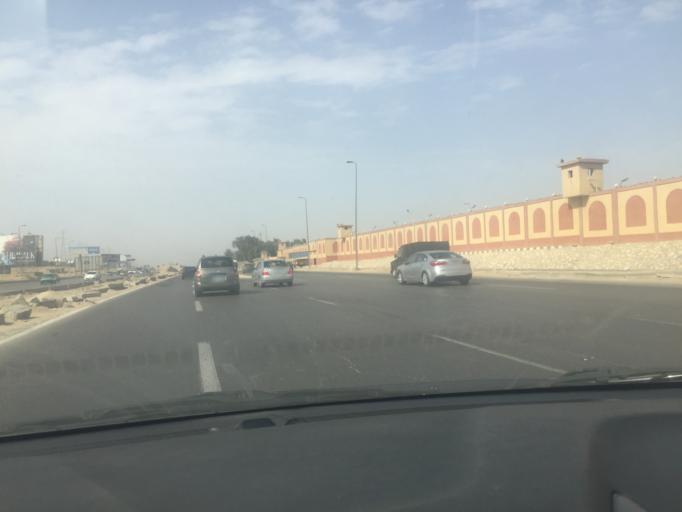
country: EG
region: Muhafazat al Qalyubiyah
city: Al Khankah
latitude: 30.0828
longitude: 31.4648
